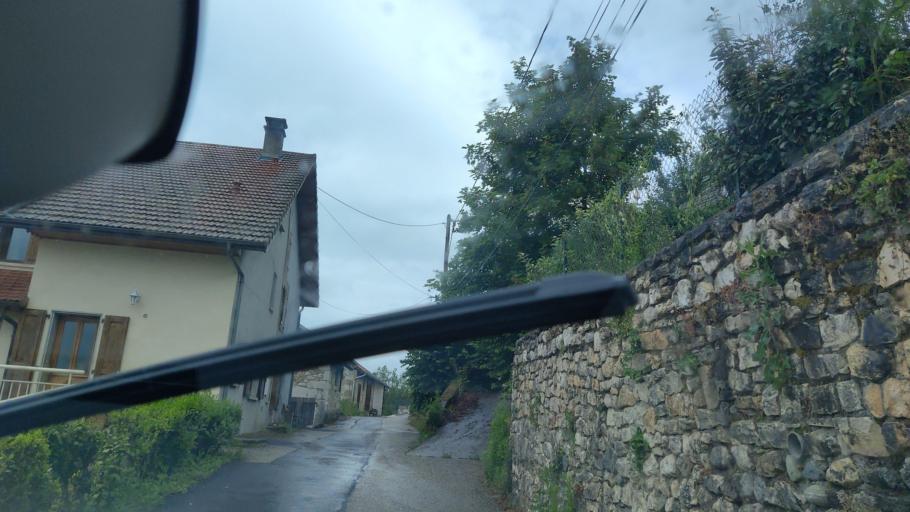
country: FR
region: Rhone-Alpes
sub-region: Departement de la Savoie
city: Chindrieux
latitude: 45.8344
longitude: 5.8479
